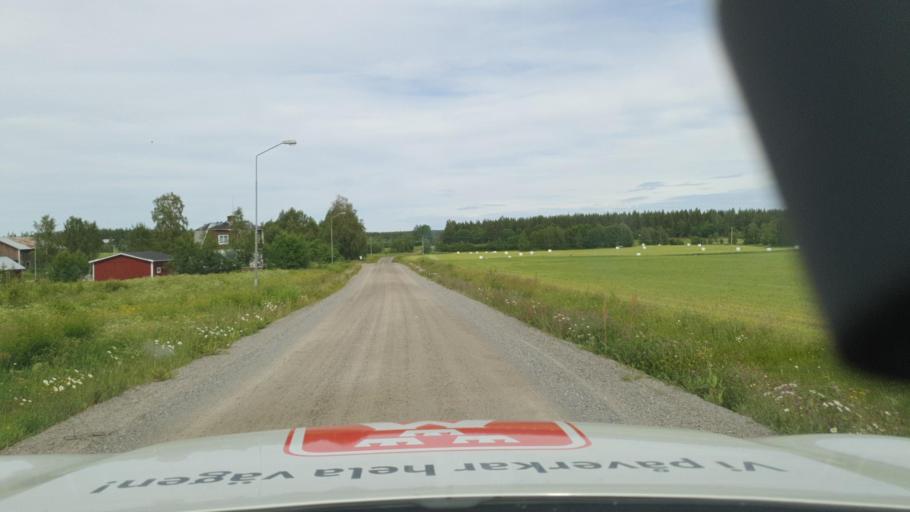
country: SE
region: Vaesterbotten
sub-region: Skelleftea Kommun
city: Viken
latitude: 64.5111
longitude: 20.9391
